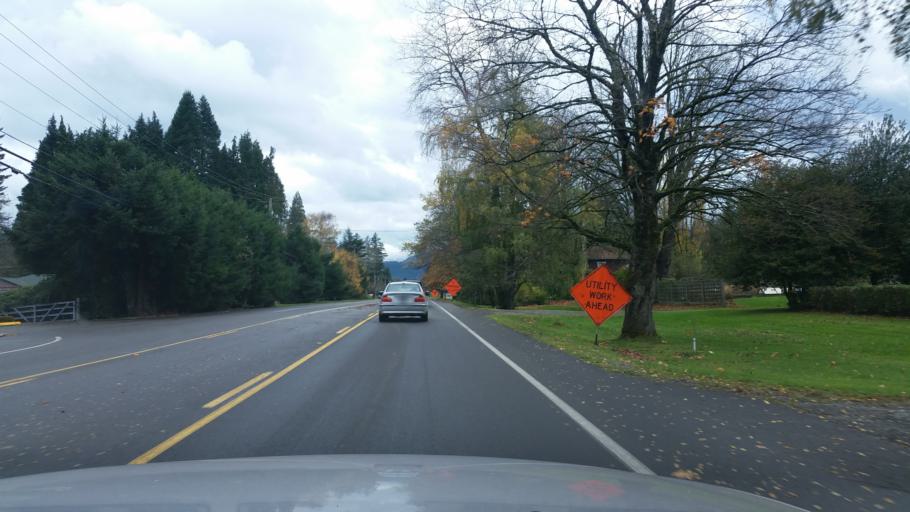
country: US
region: Washington
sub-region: King County
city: North Bend
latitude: 47.4904
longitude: -121.7774
